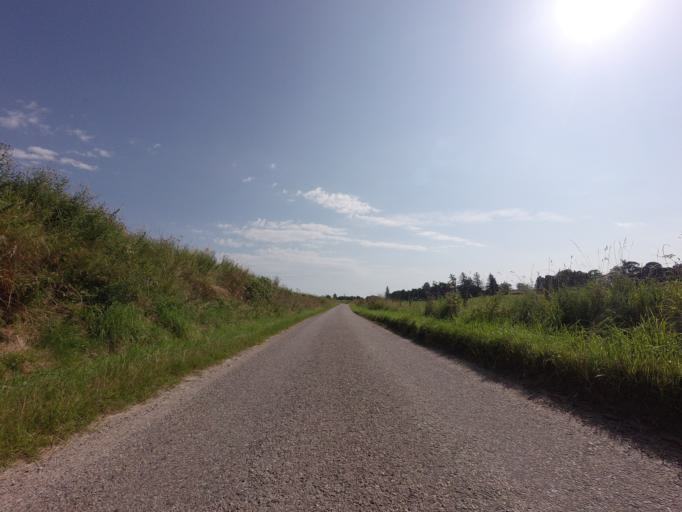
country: GB
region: Scotland
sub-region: Highland
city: Alness
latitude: 57.7064
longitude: -4.2432
